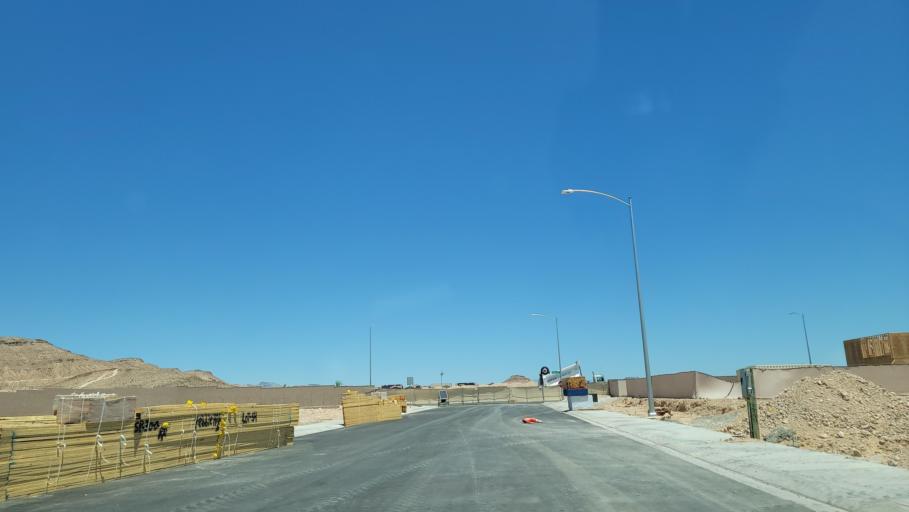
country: US
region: Nevada
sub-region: Clark County
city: Enterprise
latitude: 36.0254
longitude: -115.3031
